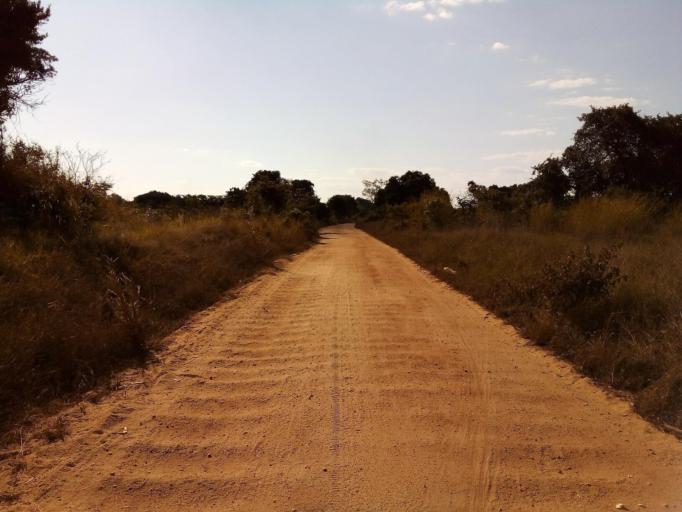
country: MZ
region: Zambezia
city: Quelimane
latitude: -17.5467
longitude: 36.6278
